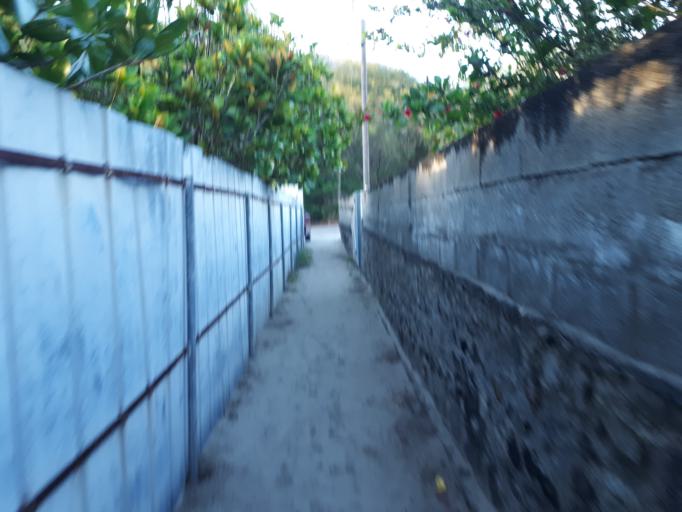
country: MQ
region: Martinique
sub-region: Martinique
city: Les Trois-Ilets
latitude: 14.5056
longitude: -61.0848
